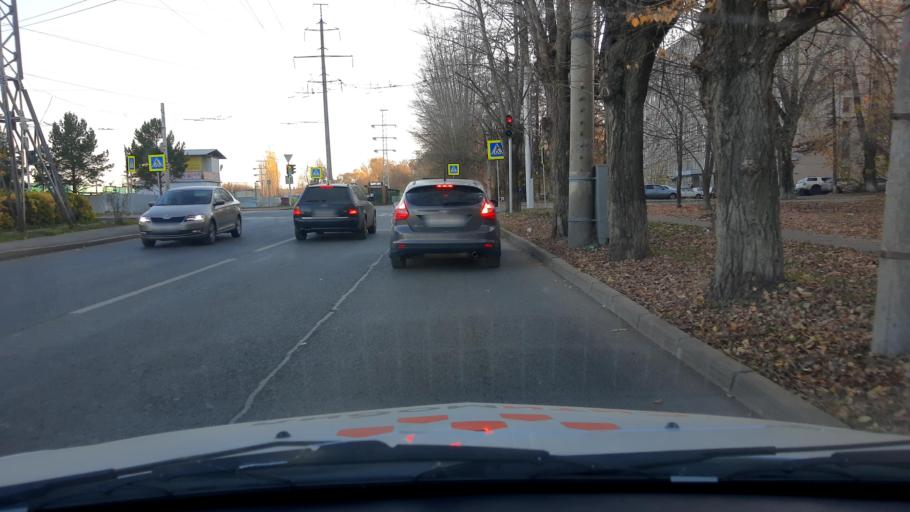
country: RU
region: Bashkortostan
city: Ufa
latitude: 54.7933
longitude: 56.0554
